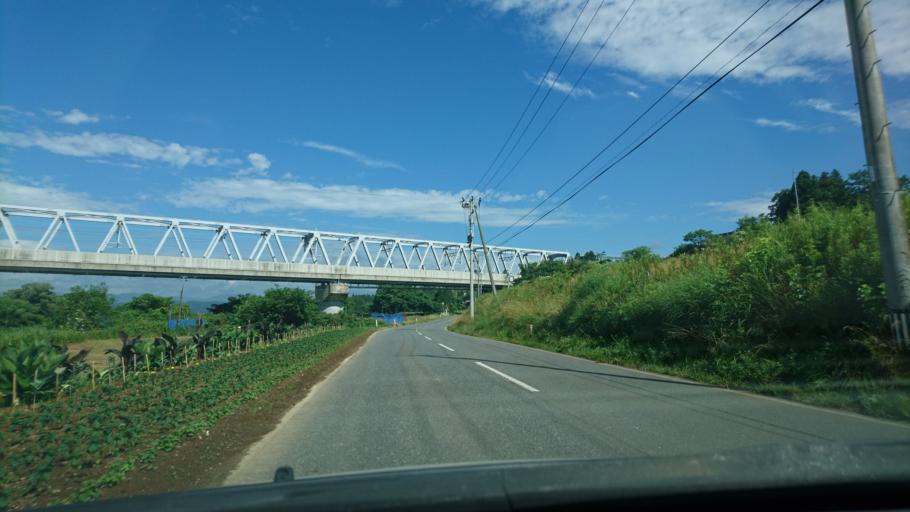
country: JP
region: Iwate
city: Ichinoseki
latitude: 38.9749
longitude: 141.1580
